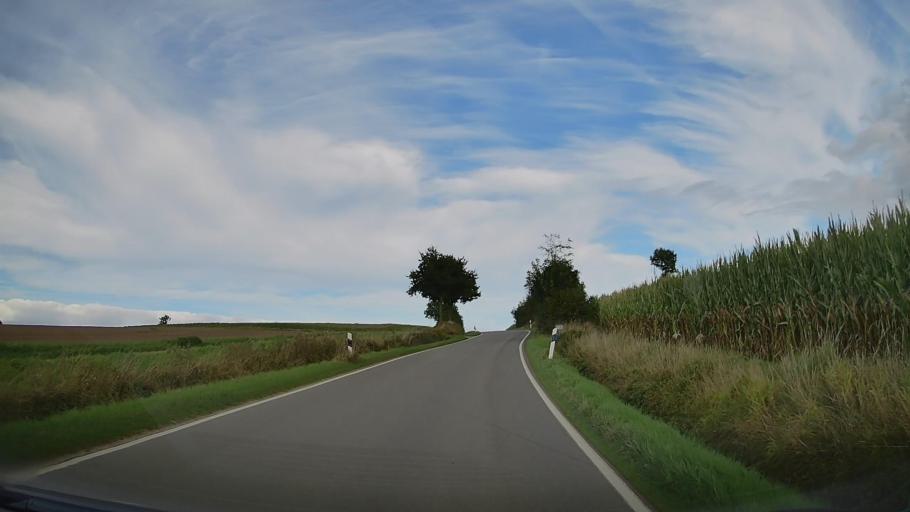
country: DE
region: Schleswig-Holstein
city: Steinberg
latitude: 54.7812
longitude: 9.7915
